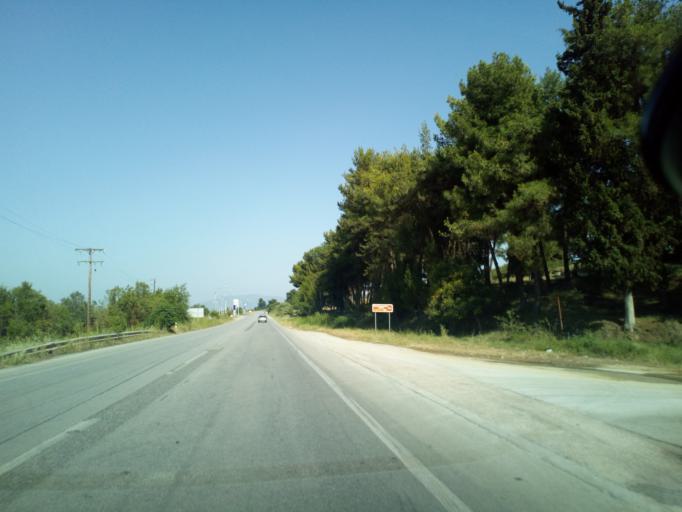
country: GR
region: Central Macedonia
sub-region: Nomos Thessalonikis
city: Nea Apollonia
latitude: 40.6560
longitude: 23.4048
